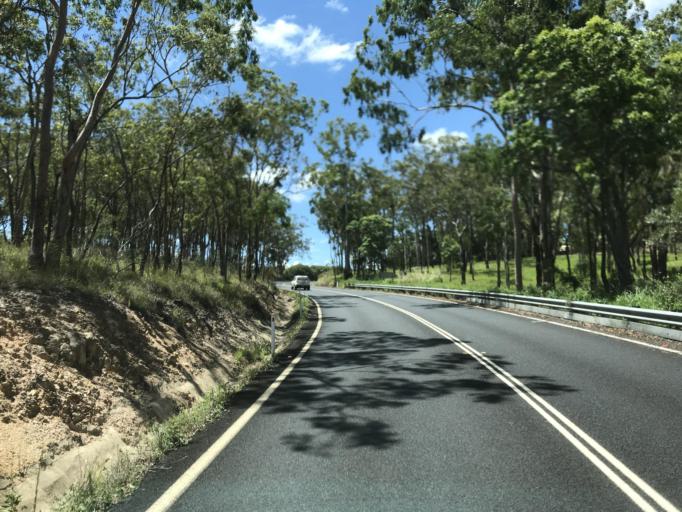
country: AU
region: Queensland
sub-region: Tablelands
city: Atherton
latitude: -17.3983
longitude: 145.3898
